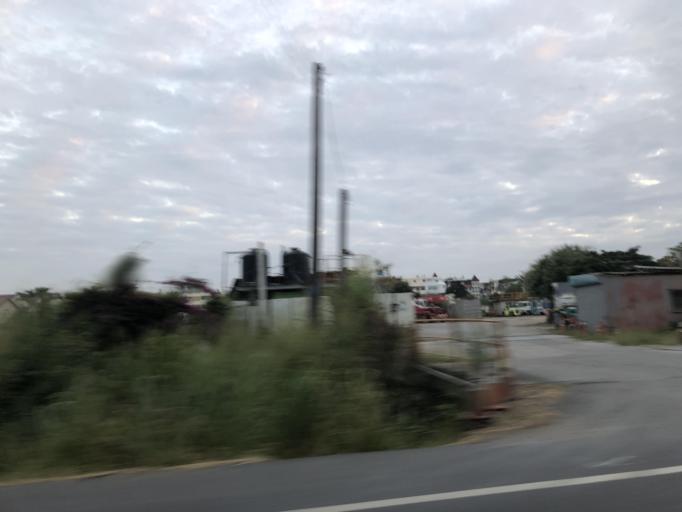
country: TW
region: Taiwan
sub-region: Tainan
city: Tainan
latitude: 23.0228
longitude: 120.3021
